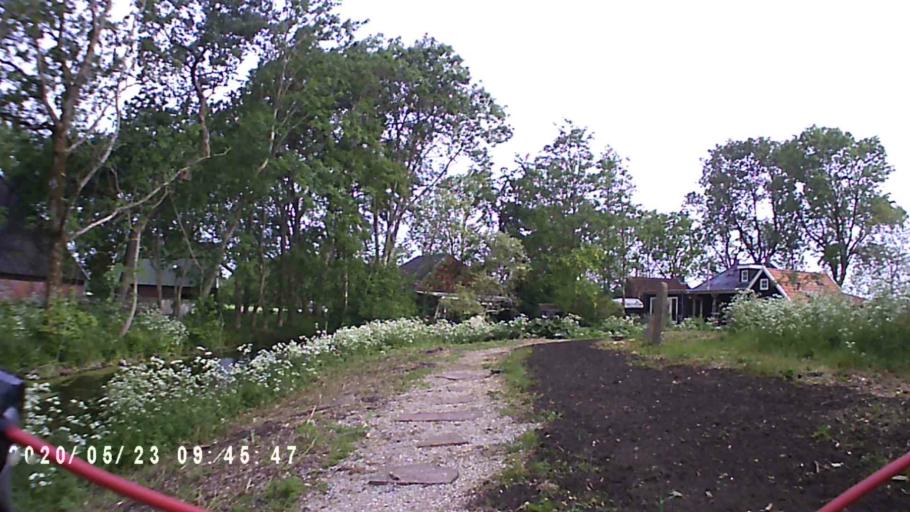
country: NL
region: Groningen
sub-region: Gemeente Slochteren
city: Slochteren
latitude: 53.2872
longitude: 6.7476
